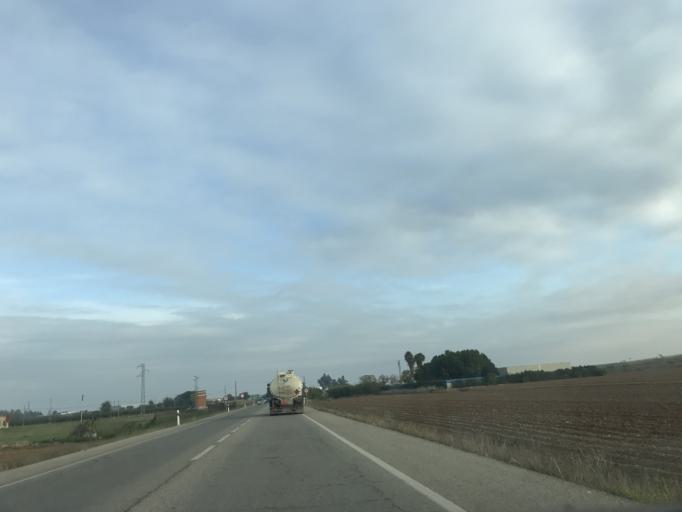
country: ES
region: Andalusia
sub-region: Provincia de Sevilla
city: La Rinconada
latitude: 37.4649
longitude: -5.9724
